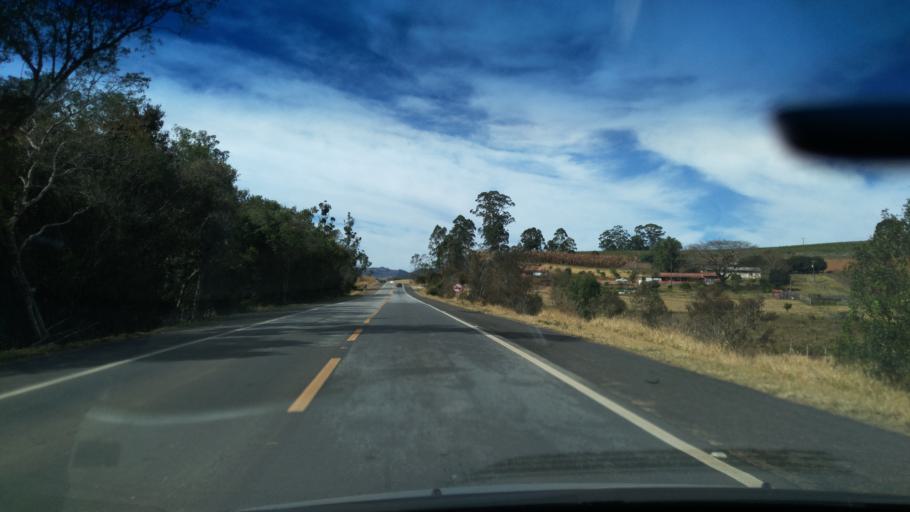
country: BR
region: Minas Gerais
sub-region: Borda Da Mata
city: Borda da Mata
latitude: -22.0586
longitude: -46.2836
